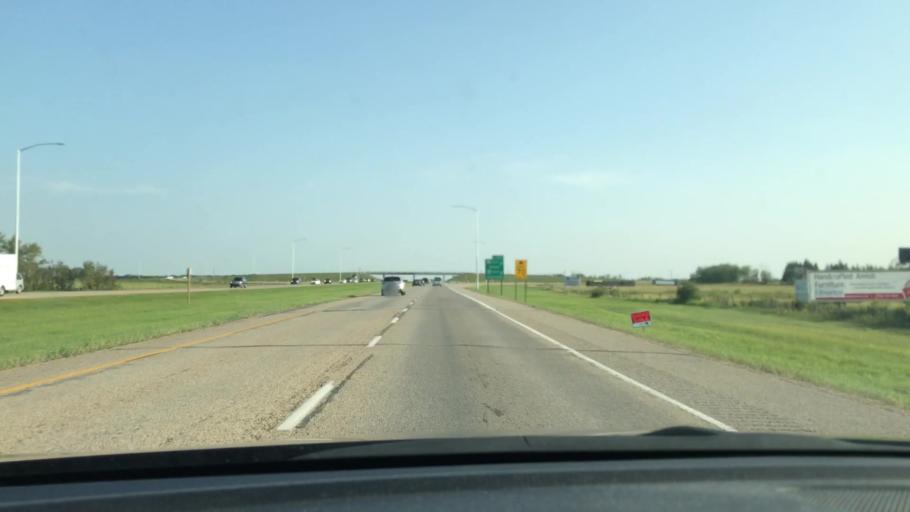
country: CA
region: Alberta
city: Millet
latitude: 53.0966
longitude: -113.5983
